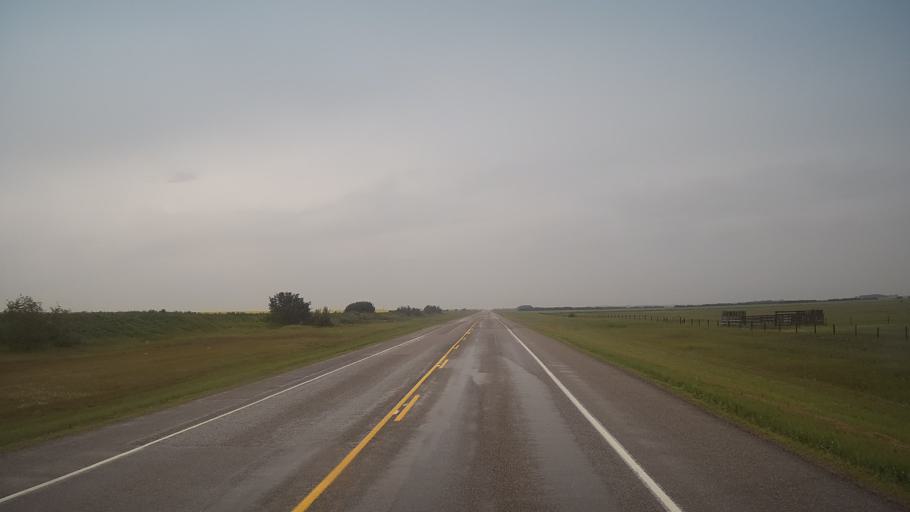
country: CA
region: Saskatchewan
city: Wilkie
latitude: 52.2181
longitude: -108.5093
